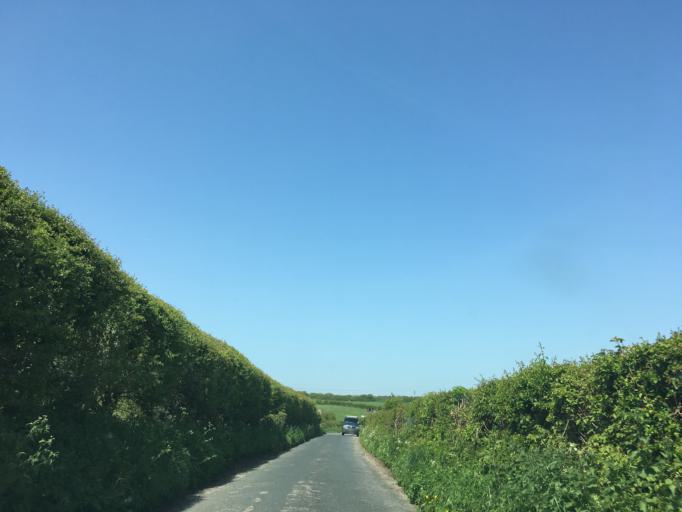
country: GB
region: England
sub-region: Isle of Wight
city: Niton
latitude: 50.5909
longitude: -1.2461
